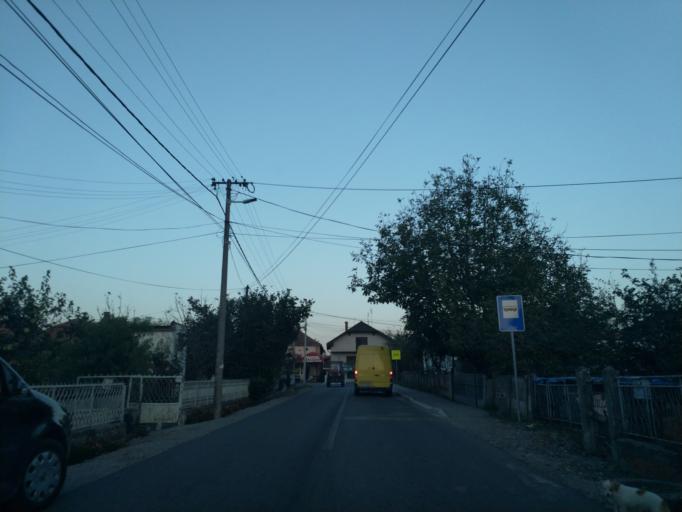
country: RS
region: Central Serbia
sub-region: Rasinski Okrug
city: Krusevac
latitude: 43.6117
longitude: 21.2955
